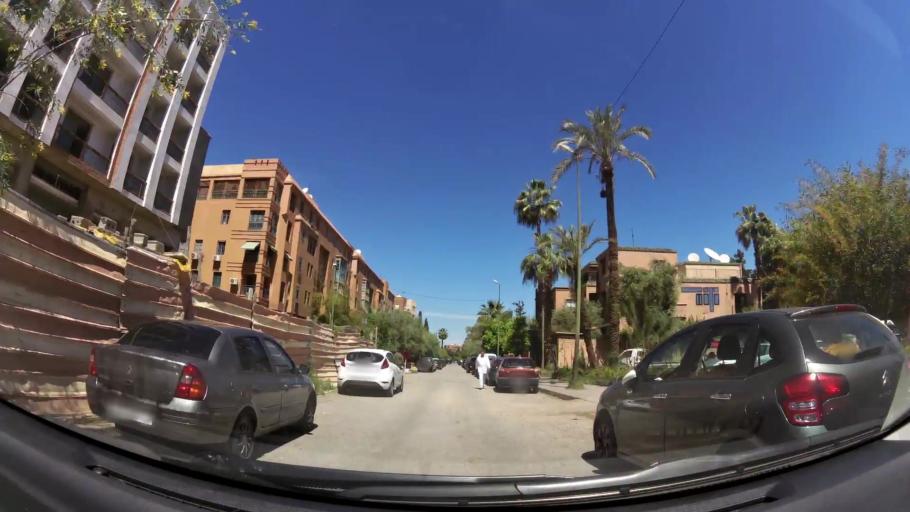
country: MA
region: Marrakech-Tensift-Al Haouz
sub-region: Marrakech
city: Marrakesh
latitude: 31.6227
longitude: -8.0011
